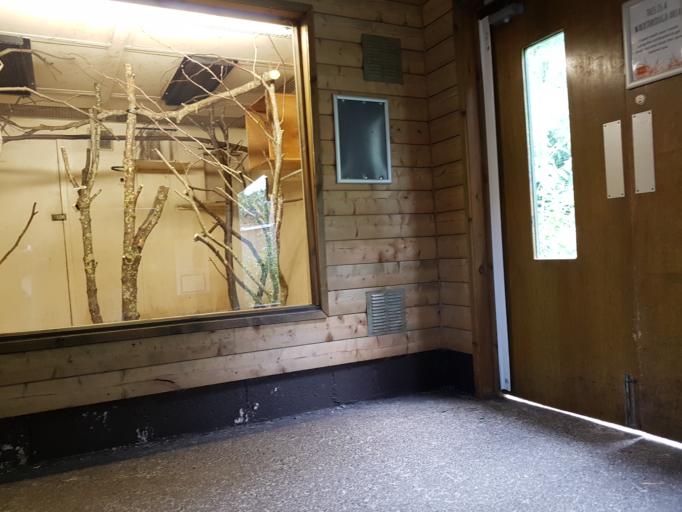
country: GB
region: Scotland
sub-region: Edinburgh
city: Colinton
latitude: 55.9432
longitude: -3.2689
